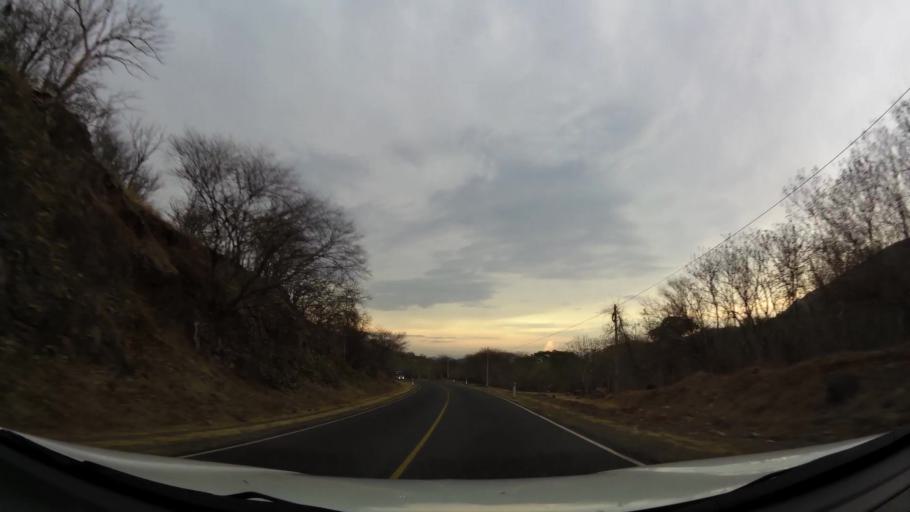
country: NI
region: Leon
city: La Jicaral
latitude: 12.6911
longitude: -86.4092
